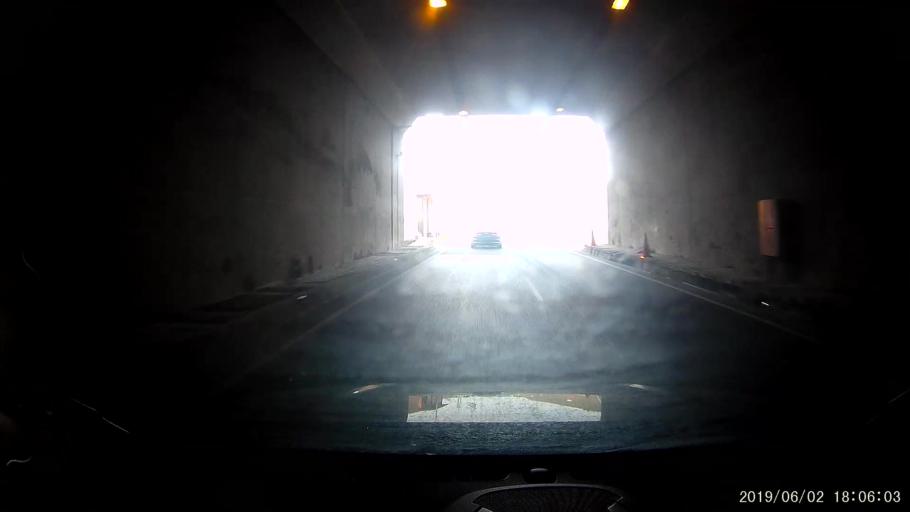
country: TR
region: Ordu
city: Unieh
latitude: 41.1138
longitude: 37.2523
